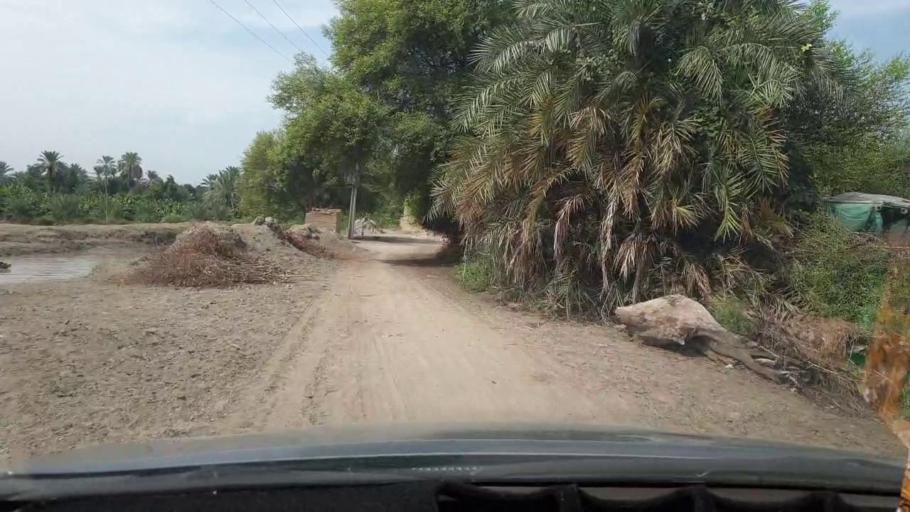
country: PK
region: Sindh
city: Khairpur
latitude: 27.5053
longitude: 68.7559
